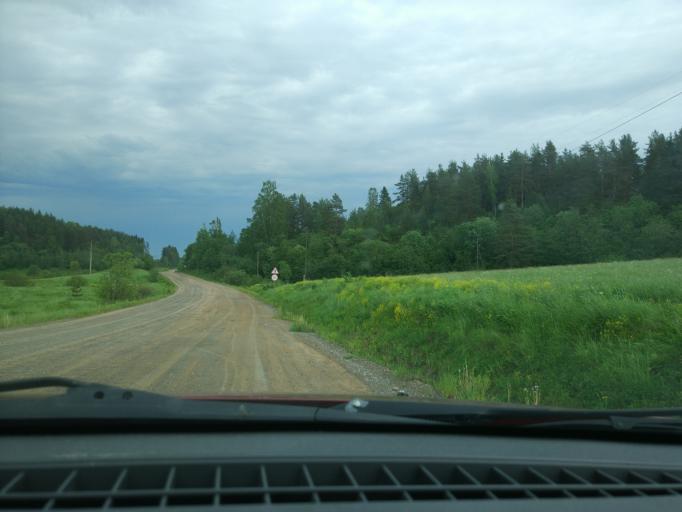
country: RU
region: Leningrad
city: Kuznechnoye
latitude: 61.2693
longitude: 29.8326
